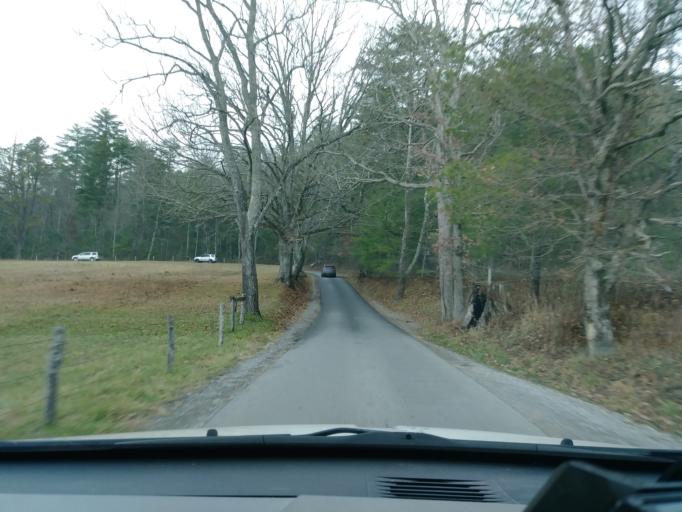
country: US
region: Tennessee
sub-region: Blount County
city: Wildwood
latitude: 35.6069
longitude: -83.8318
